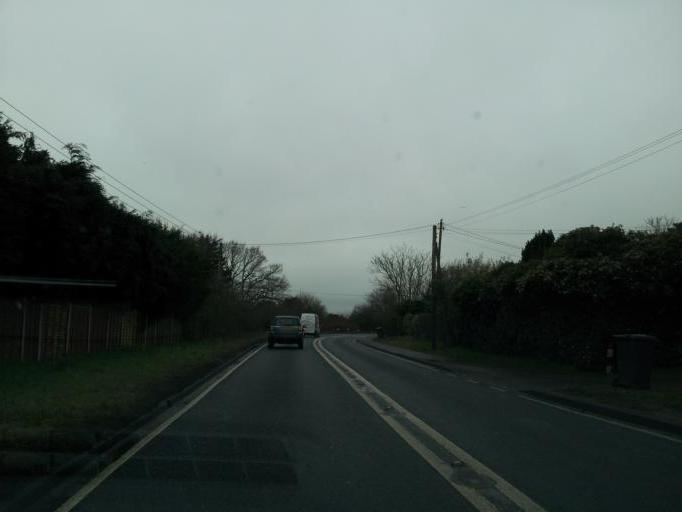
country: GB
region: England
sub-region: Essex
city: Manningtree
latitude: 51.9685
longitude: 1.0680
